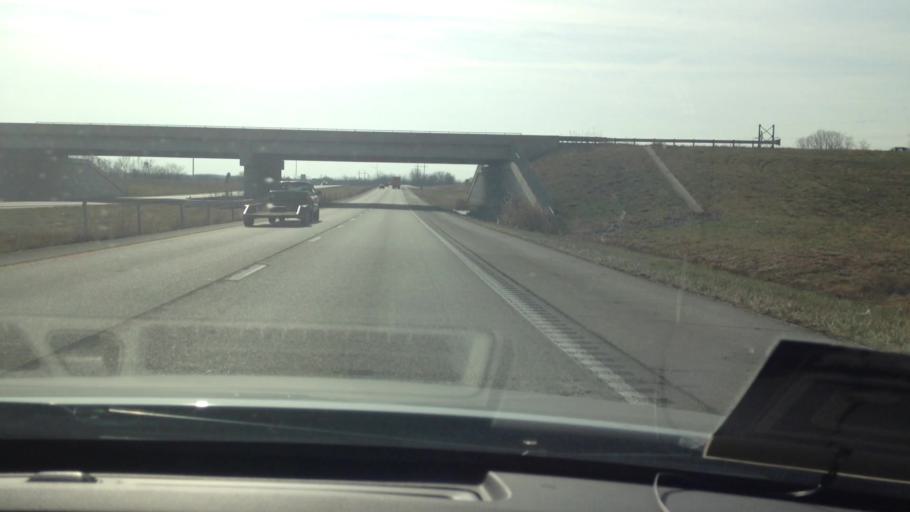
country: US
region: Missouri
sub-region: Cass County
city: Belton
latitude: 38.7871
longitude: -94.4973
